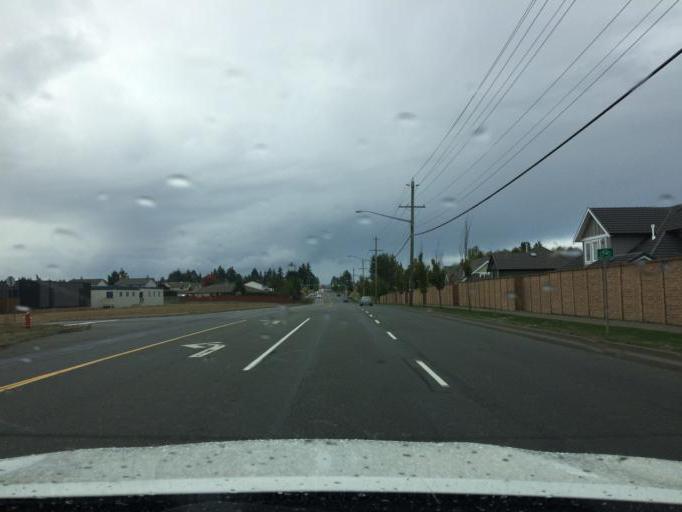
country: CA
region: British Columbia
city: Courtenay
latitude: 49.7031
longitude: -124.9565
